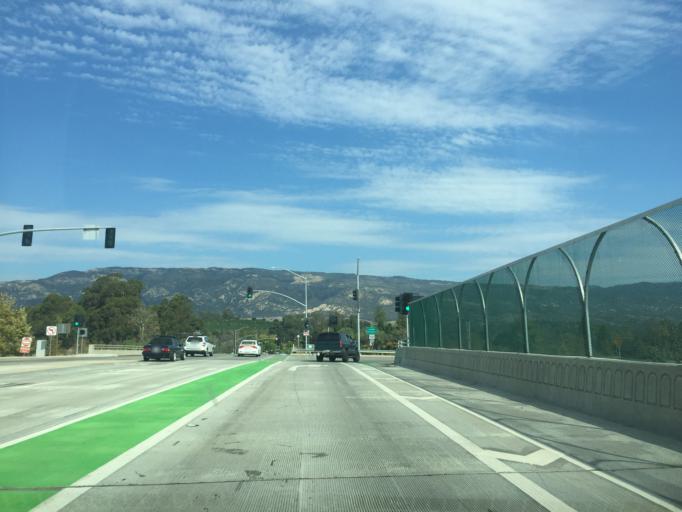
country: US
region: California
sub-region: Santa Barbara County
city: Isla Vista
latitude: 34.4367
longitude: -119.8529
